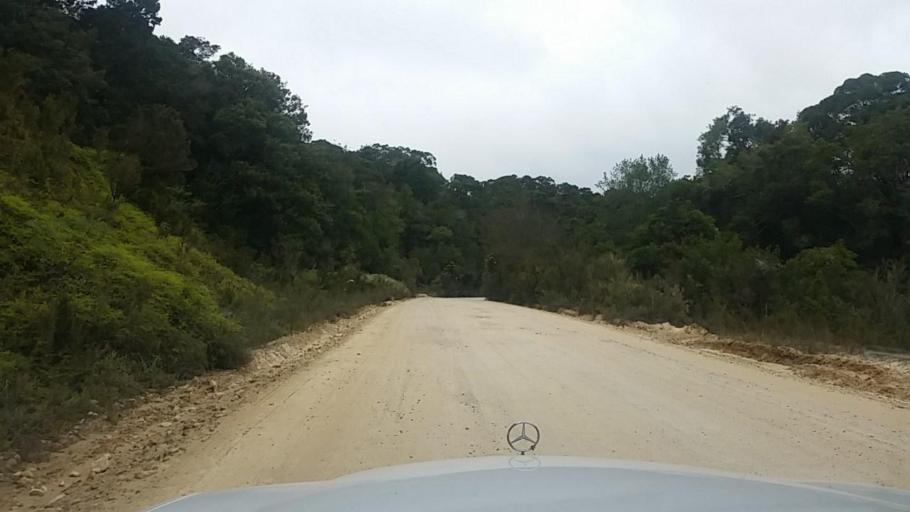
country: ZA
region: Western Cape
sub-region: Eden District Municipality
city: Knysna
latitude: -33.9605
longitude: 23.1587
